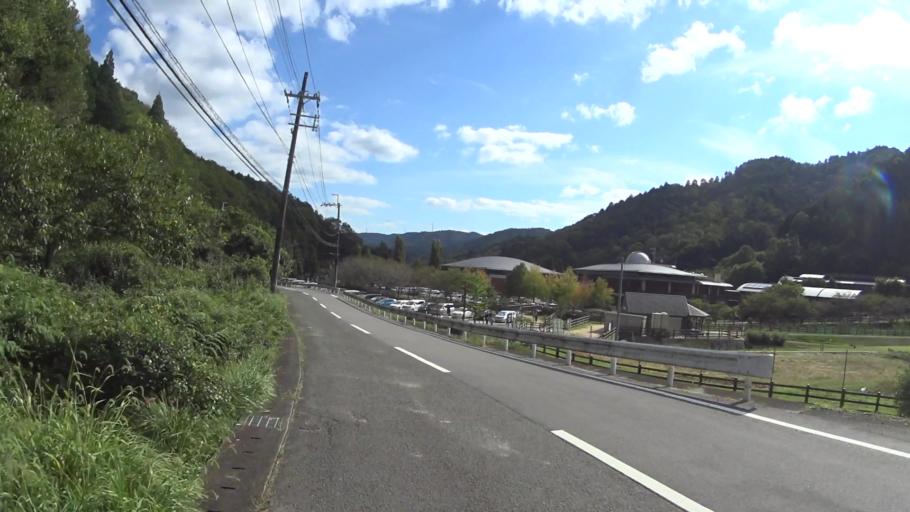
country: JP
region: Shiga Prefecture
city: Otsu-shi
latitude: 34.9355
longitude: 135.8572
